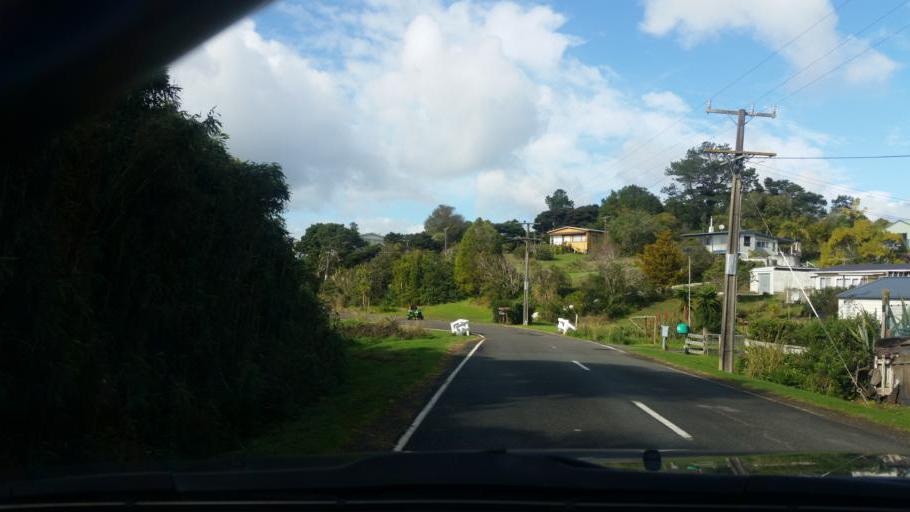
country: NZ
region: Auckland
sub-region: Auckland
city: Wellsford
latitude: -36.2546
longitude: 174.2463
